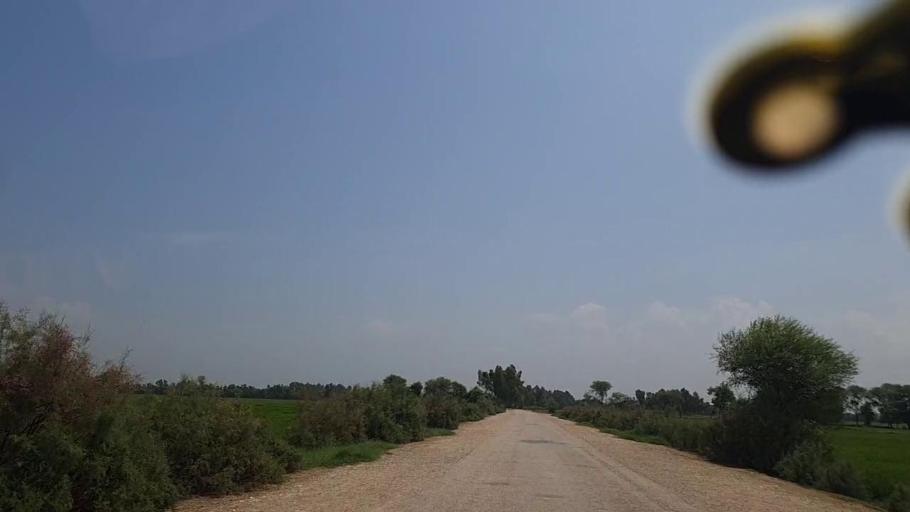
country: PK
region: Sindh
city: Rustam jo Goth
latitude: 28.1088
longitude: 68.8704
